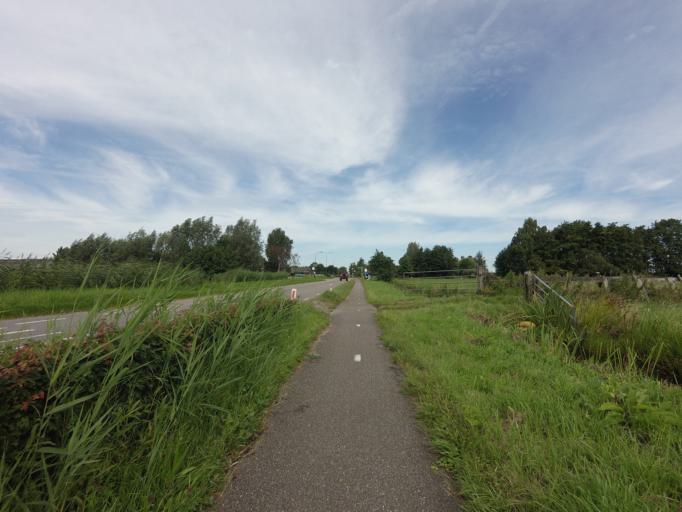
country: NL
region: Utrecht
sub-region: Stichtse Vecht
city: Breukelen
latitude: 52.1506
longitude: 4.9695
